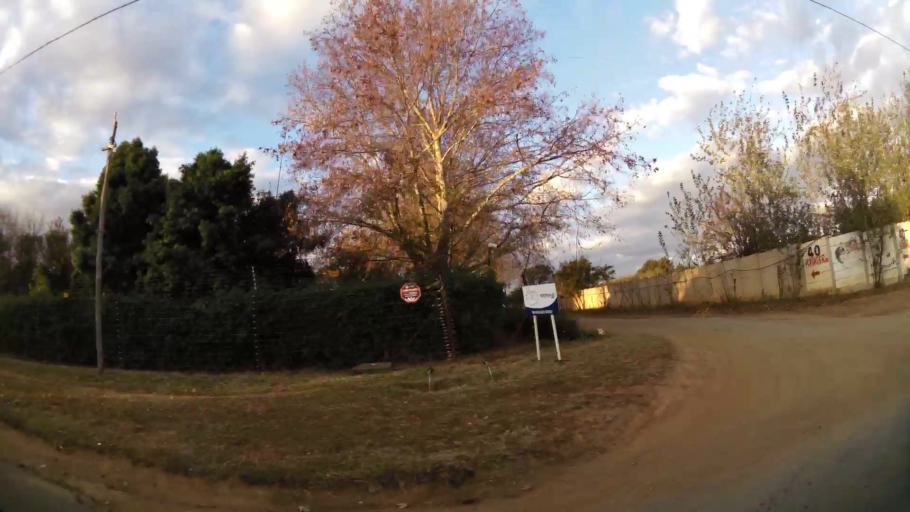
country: ZA
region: Gauteng
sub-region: City of Johannesburg Metropolitan Municipality
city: Midrand
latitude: -26.0078
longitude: 28.1537
